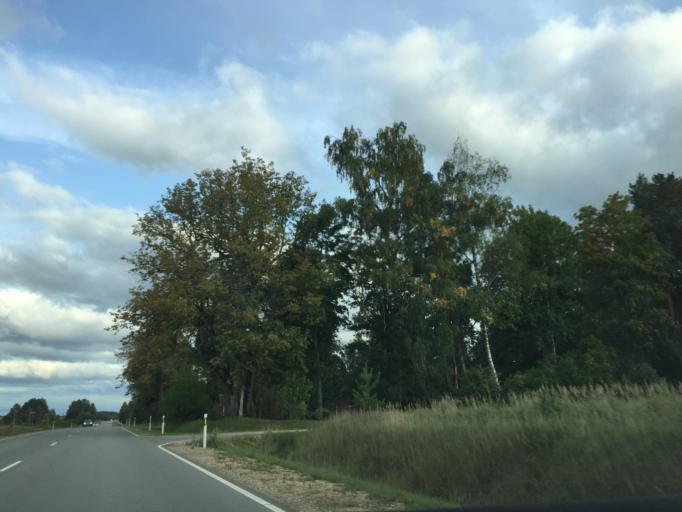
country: LV
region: Nereta
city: Nereta
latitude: 56.2434
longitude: 25.2579
